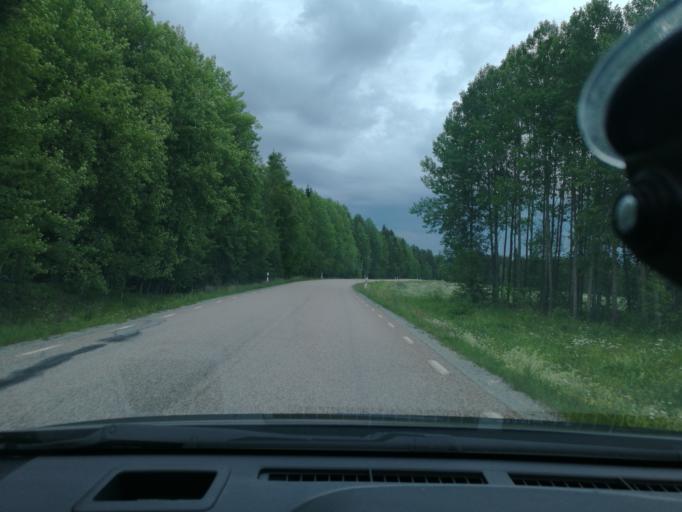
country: SE
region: Vaestmanland
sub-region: Sala Kommun
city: Sala
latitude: 59.9162
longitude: 16.4782
